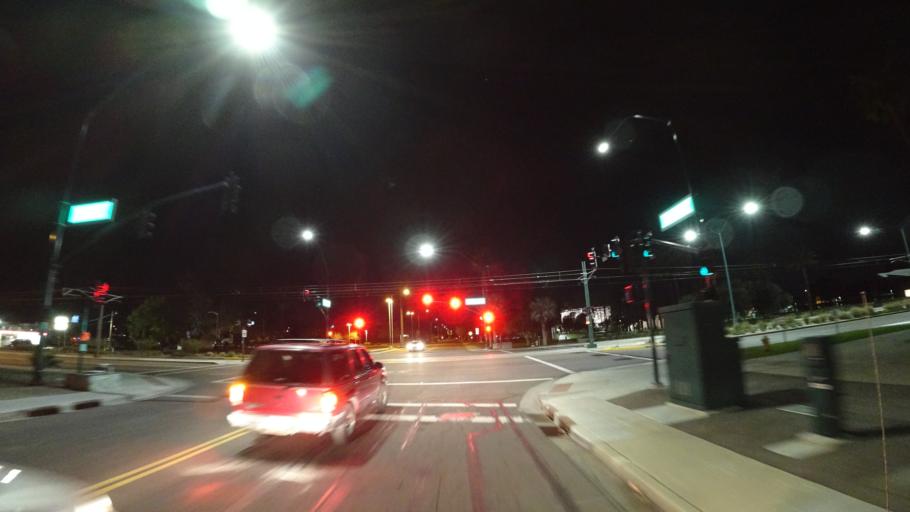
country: US
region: Arizona
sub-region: Maricopa County
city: Mesa
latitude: 33.4153
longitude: -111.8185
